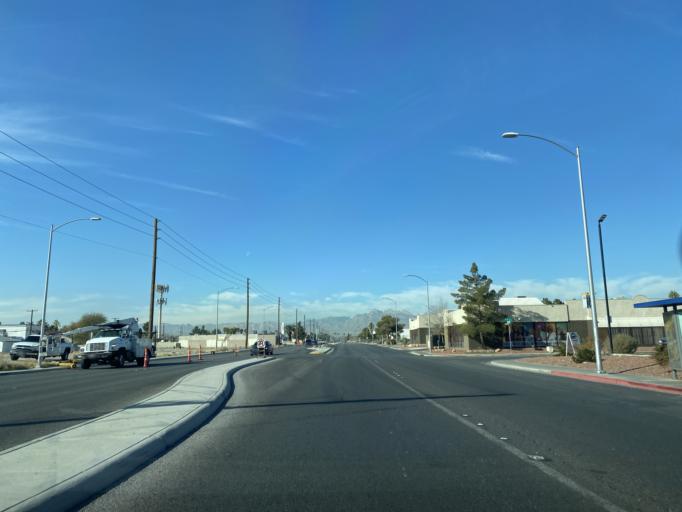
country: US
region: Nevada
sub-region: Clark County
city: Las Vegas
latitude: 36.1885
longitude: -115.1567
